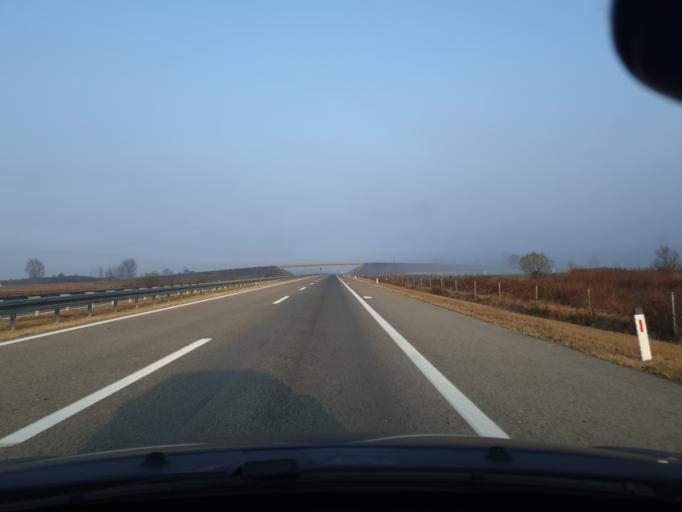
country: RS
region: Central Serbia
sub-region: Jablanicki Okrug
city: Leskovac
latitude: 43.0310
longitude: 22.0043
